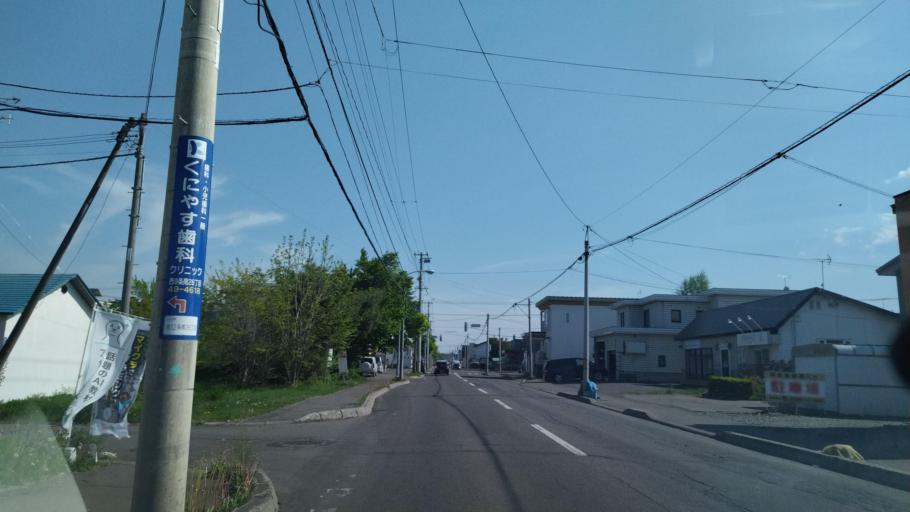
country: JP
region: Hokkaido
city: Obihiro
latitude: 42.8990
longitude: 143.1879
